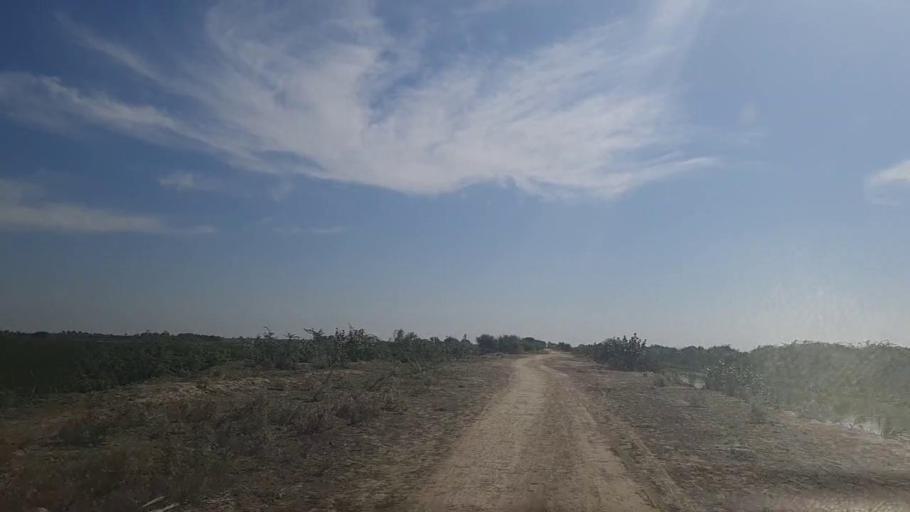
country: PK
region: Sindh
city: Mirpur Batoro
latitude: 24.6591
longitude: 68.1953
